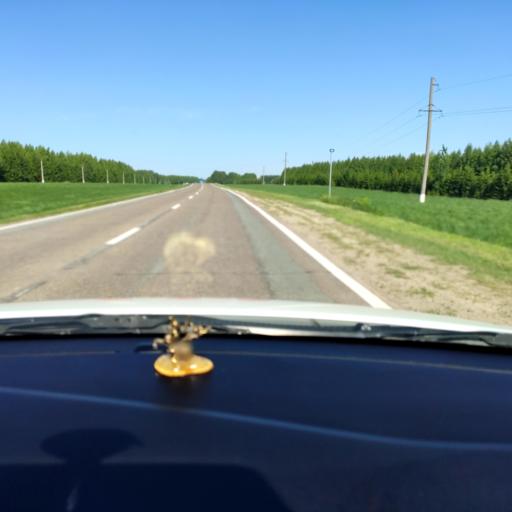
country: RU
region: Tatarstan
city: Vysokaya Gora
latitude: 56.0298
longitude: 49.2469
